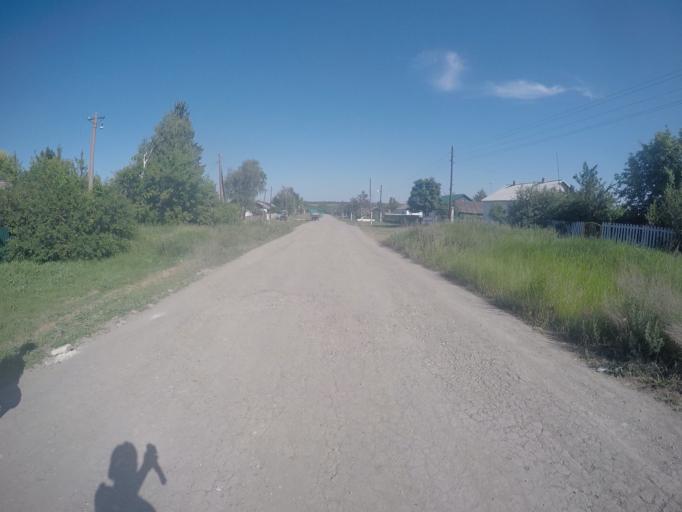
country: RU
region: Saratov
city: Krasnyy Oktyabr'
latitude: 51.2917
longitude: 45.6534
